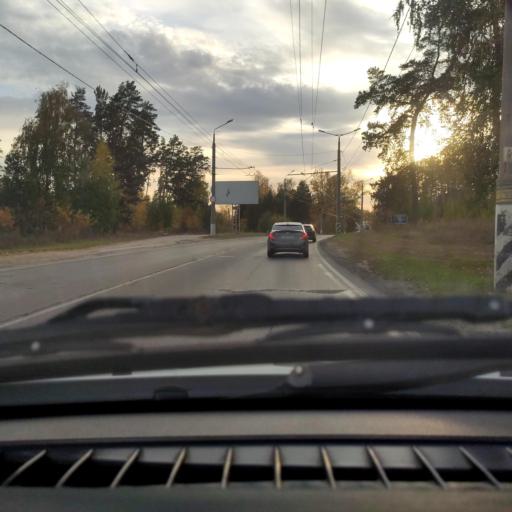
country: RU
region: Samara
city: Tol'yatti
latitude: 53.4798
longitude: 49.3727
